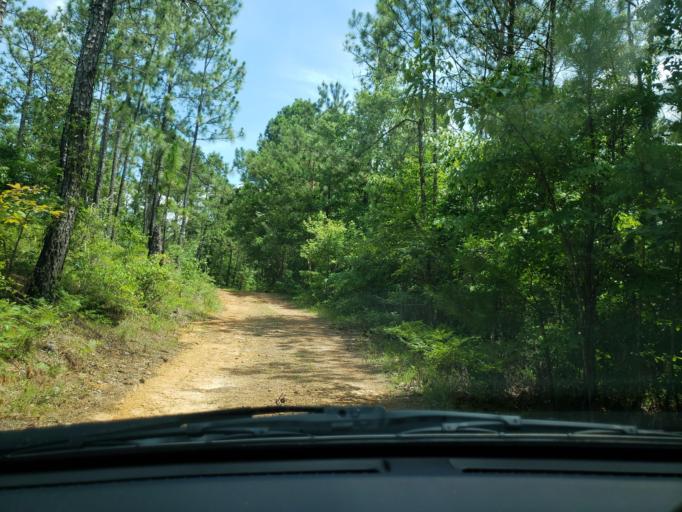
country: US
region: Alabama
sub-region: Elmore County
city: Eclectic
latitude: 32.6337
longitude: -85.9437
